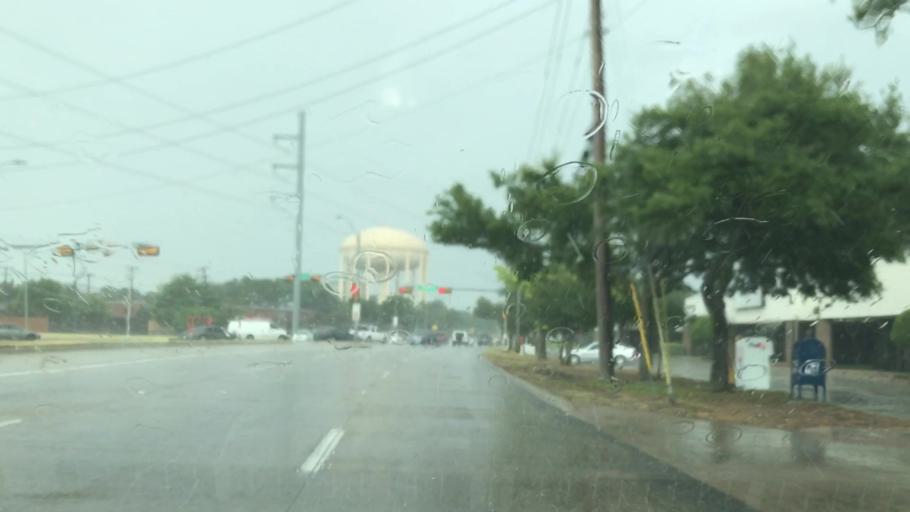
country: US
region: Texas
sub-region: Dallas County
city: Richardson
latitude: 32.9085
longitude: -96.7065
